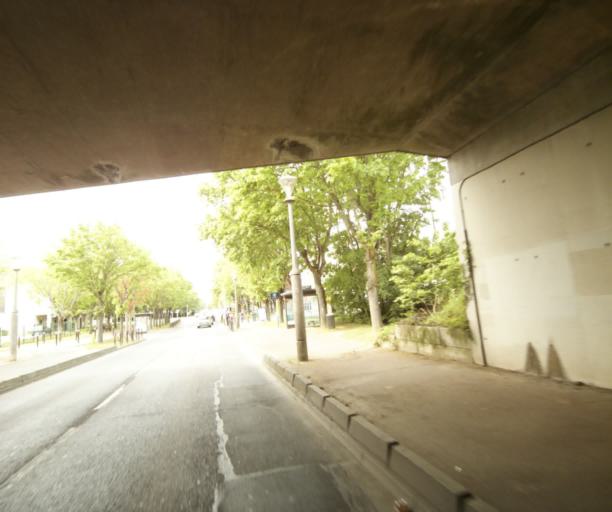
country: FR
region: Ile-de-France
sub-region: Departement de Seine-et-Marne
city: Torcy
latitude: 48.8463
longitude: 2.6527
